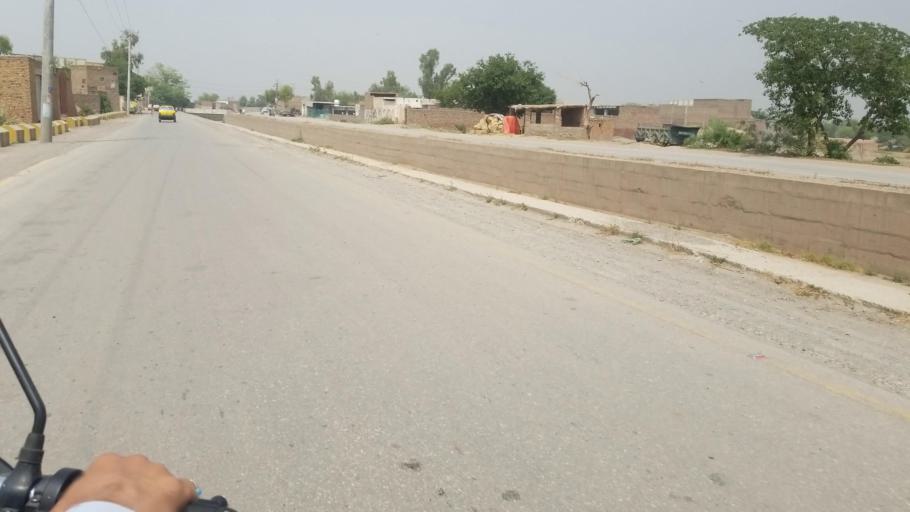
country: PK
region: Khyber Pakhtunkhwa
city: Peshawar
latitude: 33.9593
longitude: 71.5456
